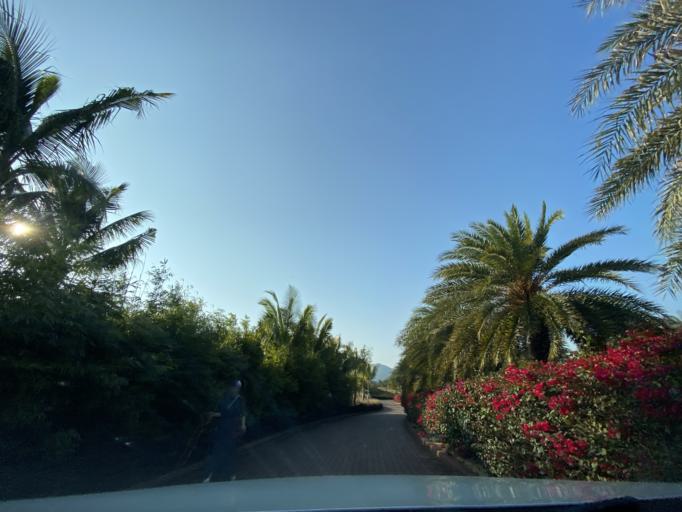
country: CN
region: Hainan
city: Xincun
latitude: 18.4175
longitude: 109.9540
